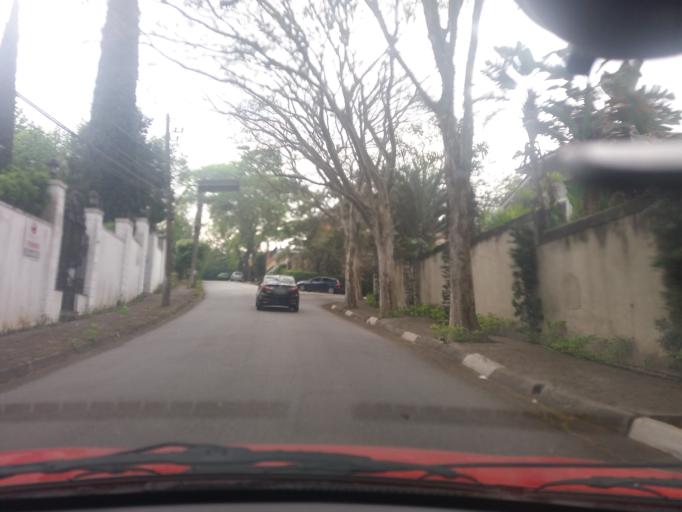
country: BR
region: Sao Paulo
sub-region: Taboao Da Serra
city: Taboao da Serra
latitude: -23.5930
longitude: -46.7128
